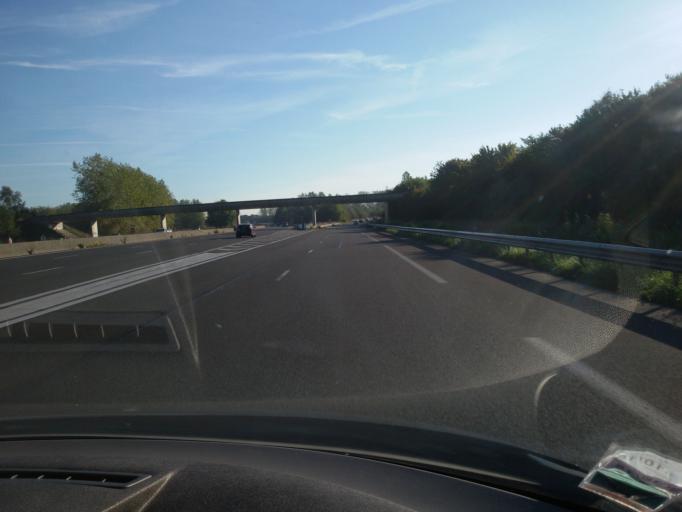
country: FR
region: Ile-de-France
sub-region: Departement de Seine-et-Marne
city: Bailly-Romainvilliers
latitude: 48.8362
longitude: 2.8104
